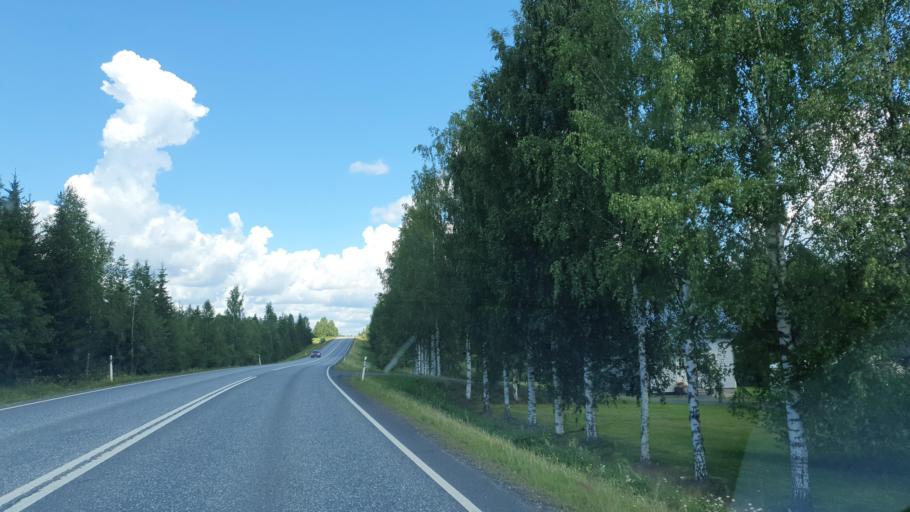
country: FI
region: Northern Savo
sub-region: Ylae-Savo
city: Sonkajaervi
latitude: 63.8052
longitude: 27.4173
